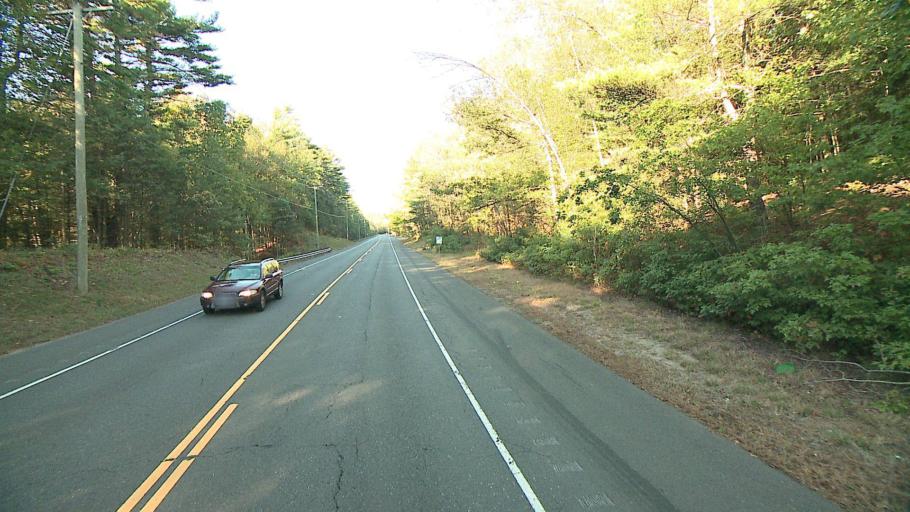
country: US
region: Connecticut
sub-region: Hartford County
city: Collinsville
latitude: 41.8203
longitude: -72.9553
